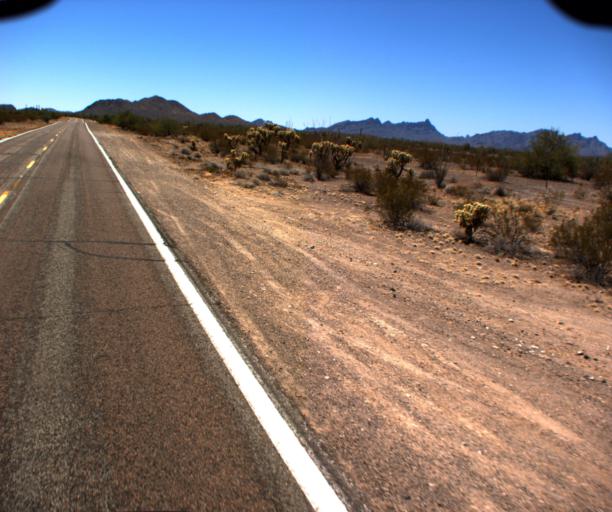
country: US
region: Arizona
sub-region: Pima County
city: Ajo
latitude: 32.2320
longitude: -112.7139
